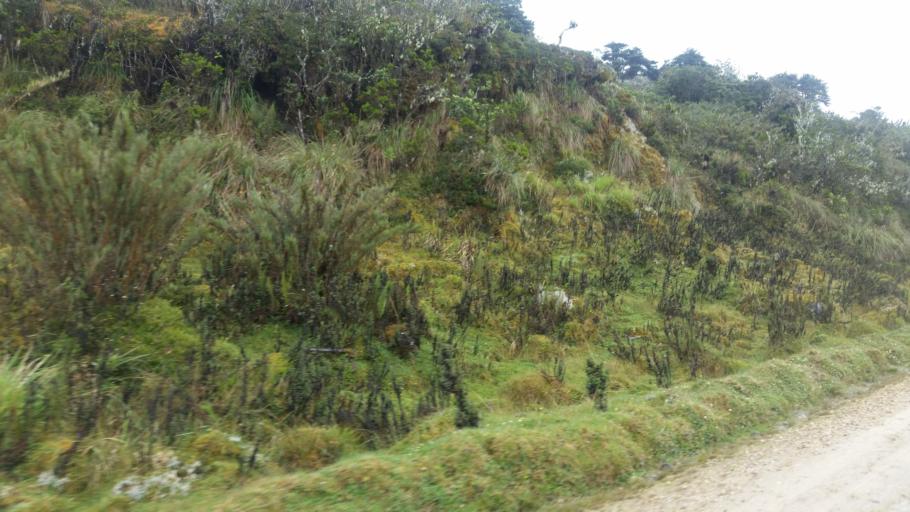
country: CO
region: Cundinamarca
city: La Calera
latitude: 4.7205
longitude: -73.8215
